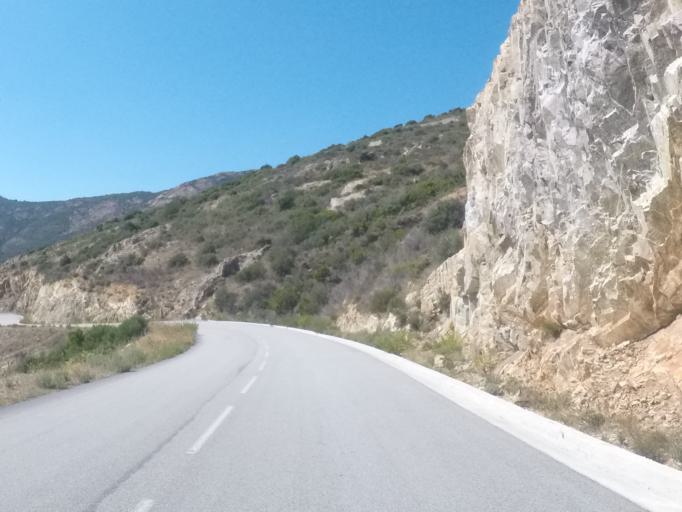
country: FR
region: Corsica
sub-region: Departement de la Haute-Corse
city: Calvi
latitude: 42.4765
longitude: 8.7545
